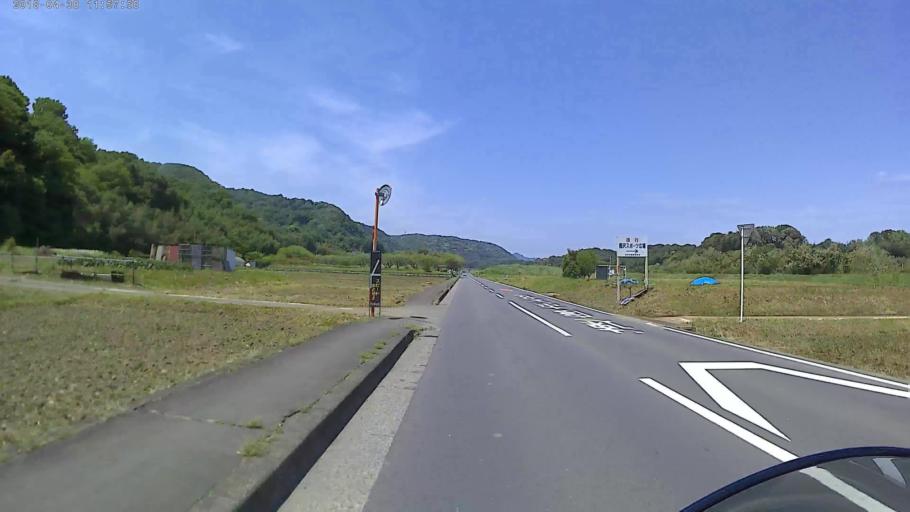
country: JP
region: Kanagawa
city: Zama
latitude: 35.4985
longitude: 139.3394
